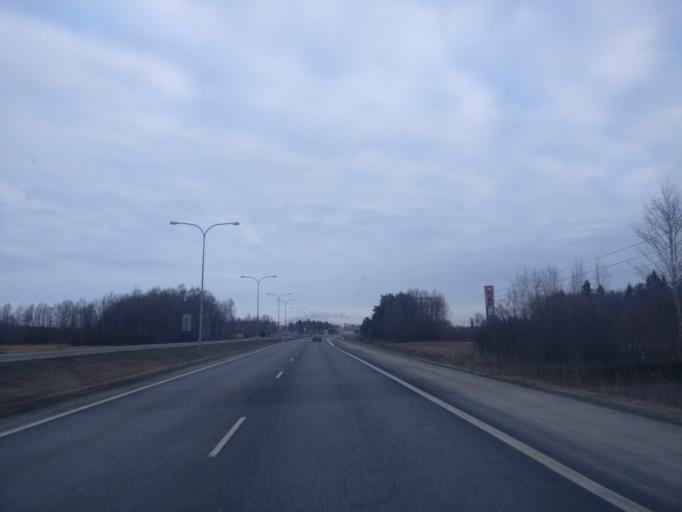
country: FI
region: Northern Ostrobothnia
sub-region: Oulu
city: Kempele
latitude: 64.9531
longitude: 25.5254
